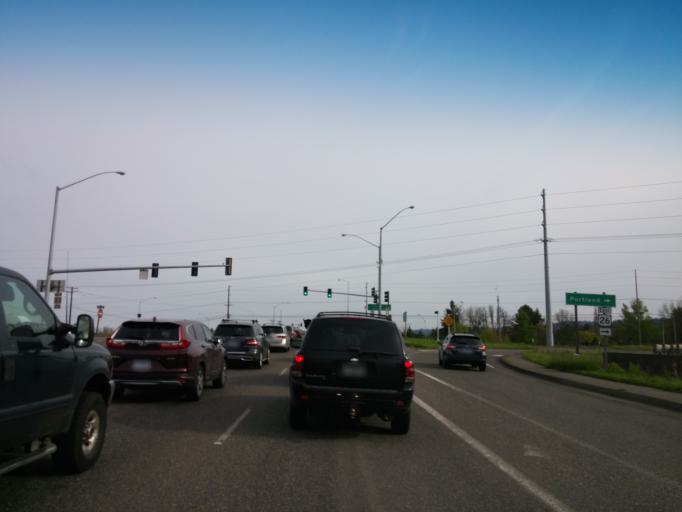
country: US
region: Oregon
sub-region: Washington County
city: Cedar Mill
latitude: 45.5208
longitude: -122.8158
